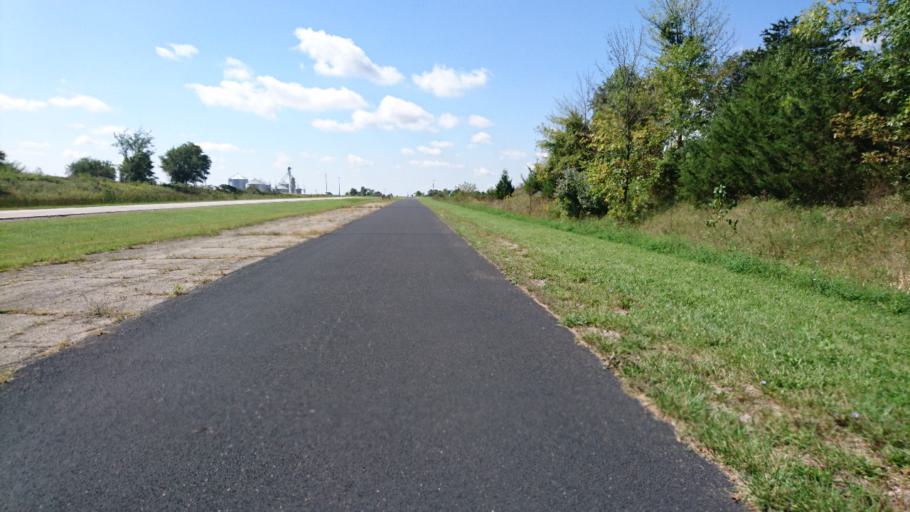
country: US
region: Illinois
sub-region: McLean County
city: Lexington
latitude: 40.6292
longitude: -88.8038
